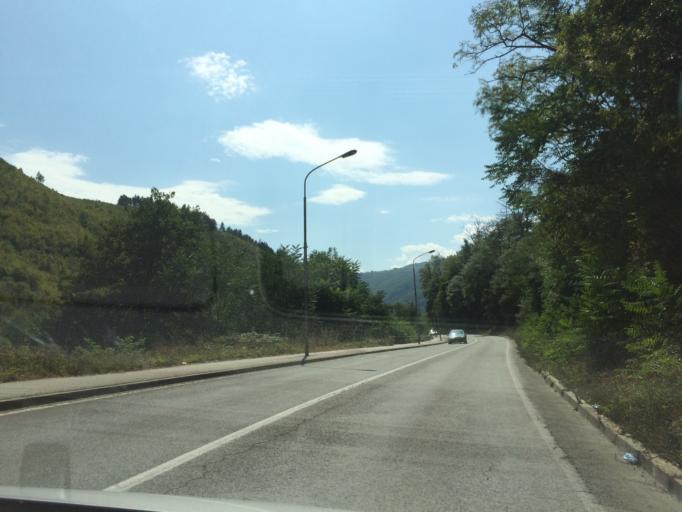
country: RS
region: Central Serbia
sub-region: Zlatiborski Okrug
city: Prijepolje
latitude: 43.3818
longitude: 19.6367
